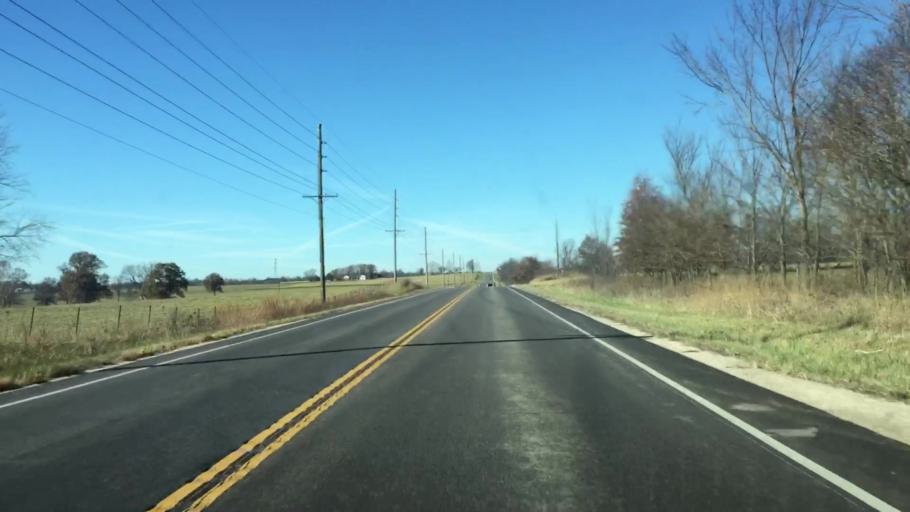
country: US
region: Missouri
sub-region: Miller County
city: Eldon
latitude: 38.3737
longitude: -92.6302
